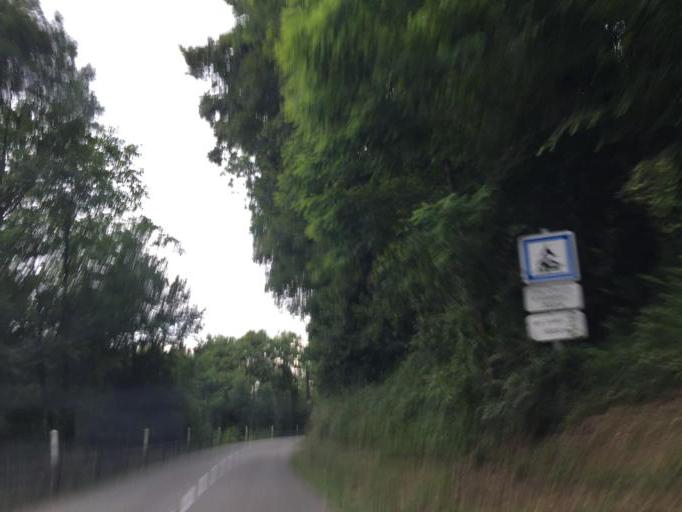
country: FR
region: Rhone-Alpes
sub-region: Departement de la Savoie
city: Le Pont-de-Beauvoisin
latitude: 45.5476
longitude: 5.6760
